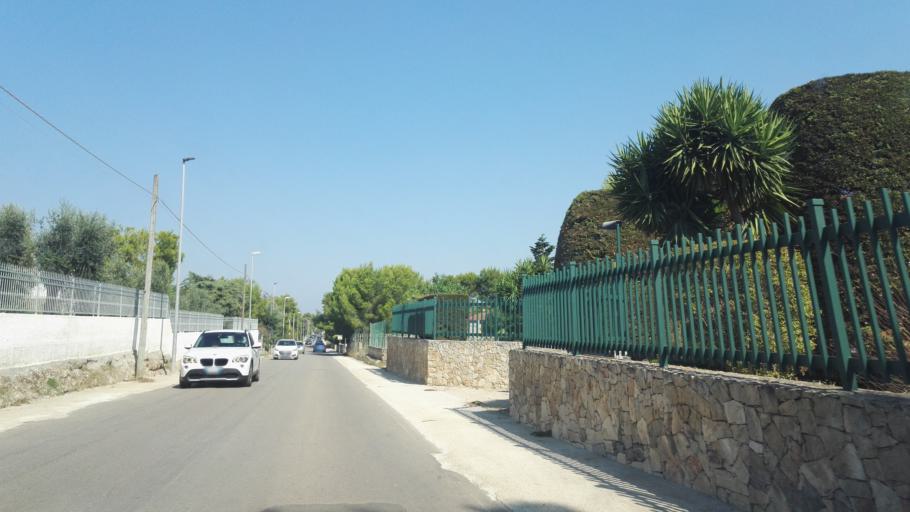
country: IT
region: Apulia
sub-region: Provincia di Lecce
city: Nardo
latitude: 40.1452
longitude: 18.0065
